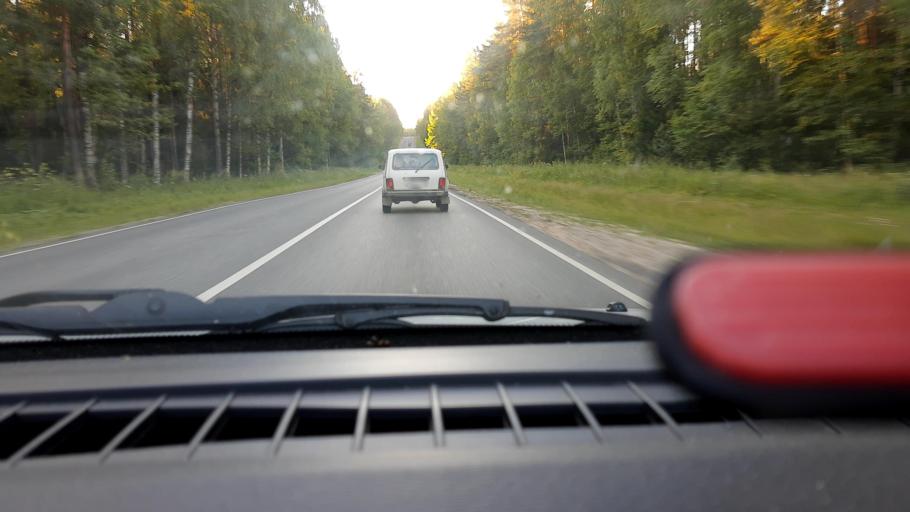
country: RU
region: Nizjnij Novgorod
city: Krasnyye Baki
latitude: 56.9930
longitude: 45.1148
